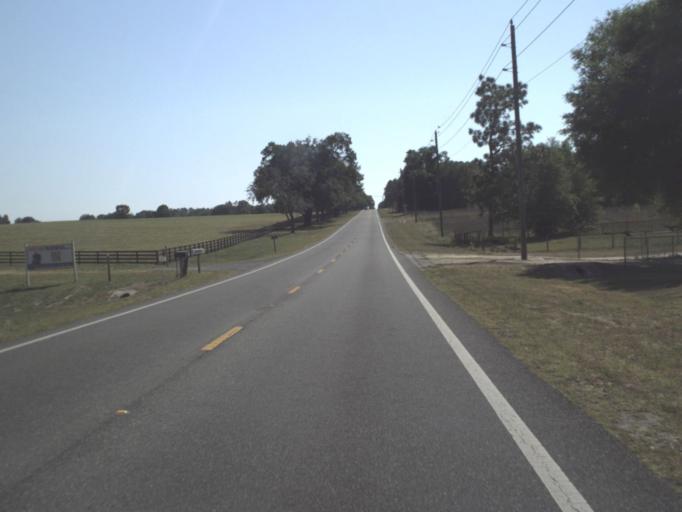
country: US
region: Florida
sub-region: Marion County
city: Dunnellon
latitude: 29.1553
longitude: -82.3571
